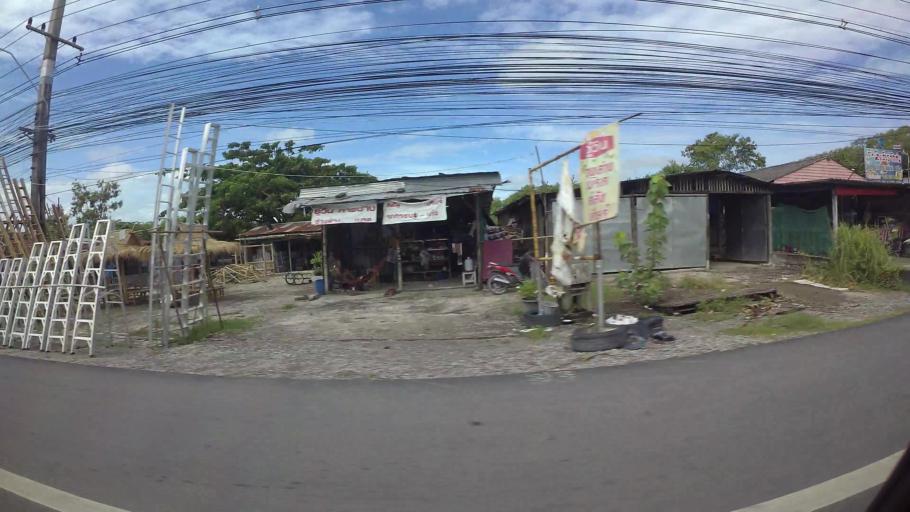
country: TH
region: Rayong
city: Ban Chang
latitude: 12.7196
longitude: 101.1575
